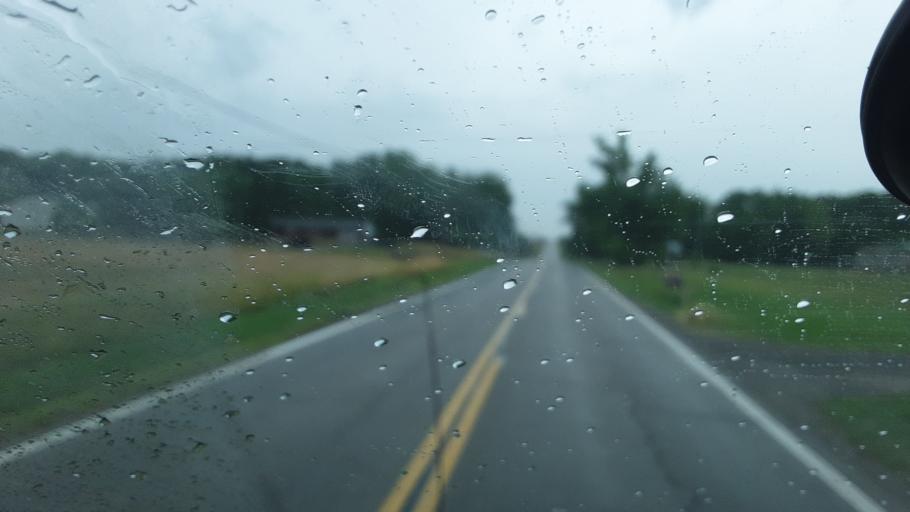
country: US
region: Ohio
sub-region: Williams County
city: Montpelier
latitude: 41.5190
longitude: -84.6129
